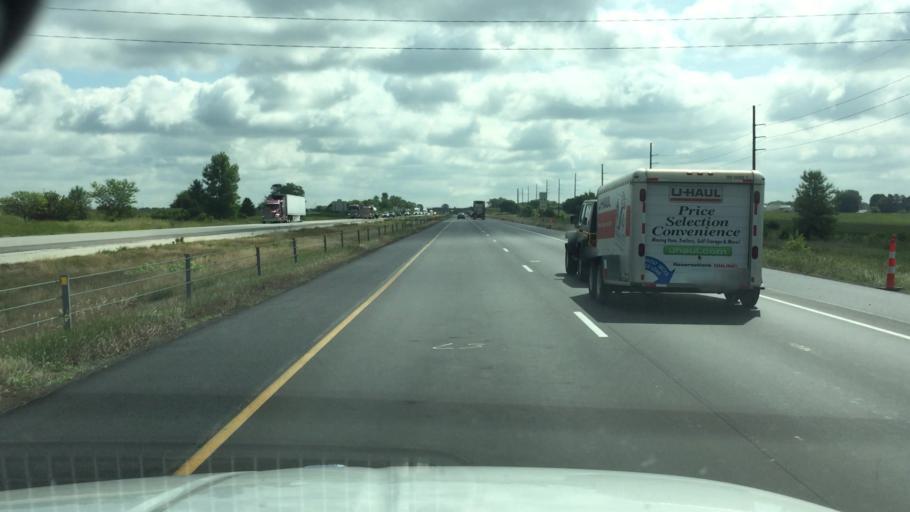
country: US
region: Iowa
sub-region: Scott County
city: Eldridge
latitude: 41.5997
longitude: -90.6084
